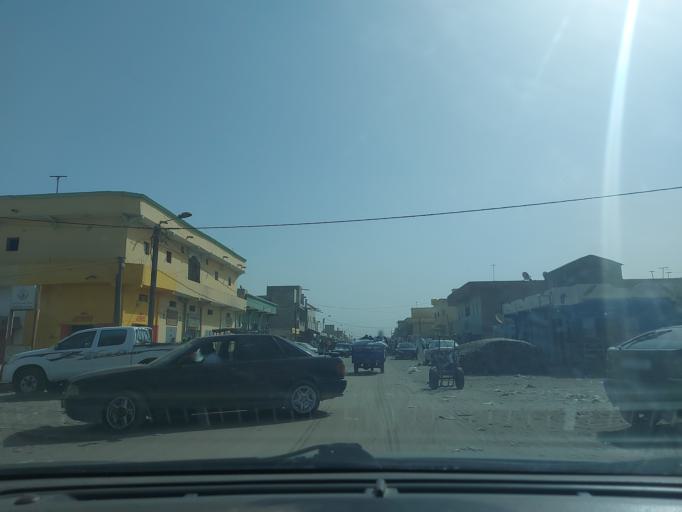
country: MR
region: Nouakchott
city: Nouakchott
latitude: 18.0721
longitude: -15.9931
